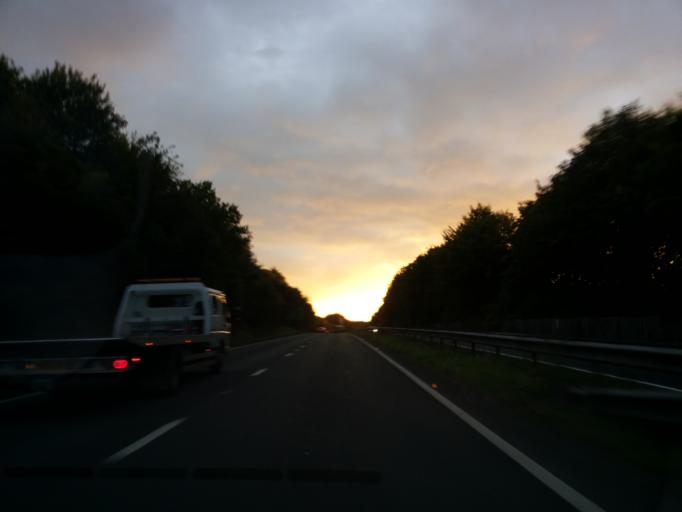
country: GB
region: England
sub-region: Hampshire
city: Abbotts Ann
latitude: 51.2085
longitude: -1.5807
